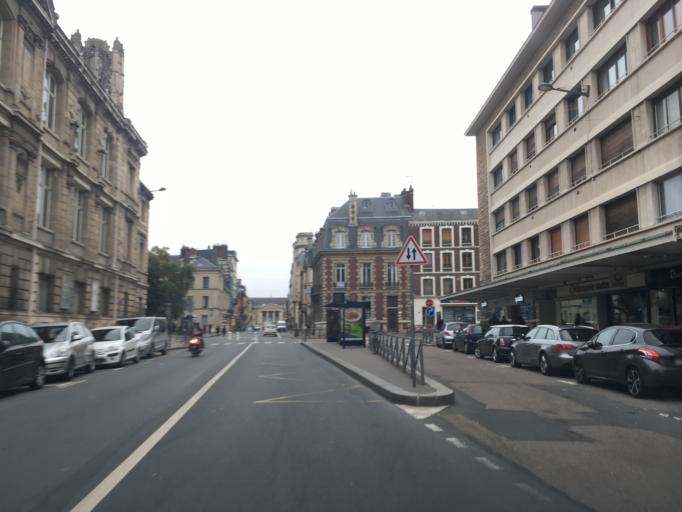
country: FR
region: Haute-Normandie
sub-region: Departement de la Seine-Maritime
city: Rouen
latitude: 49.4443
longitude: 1.0939
